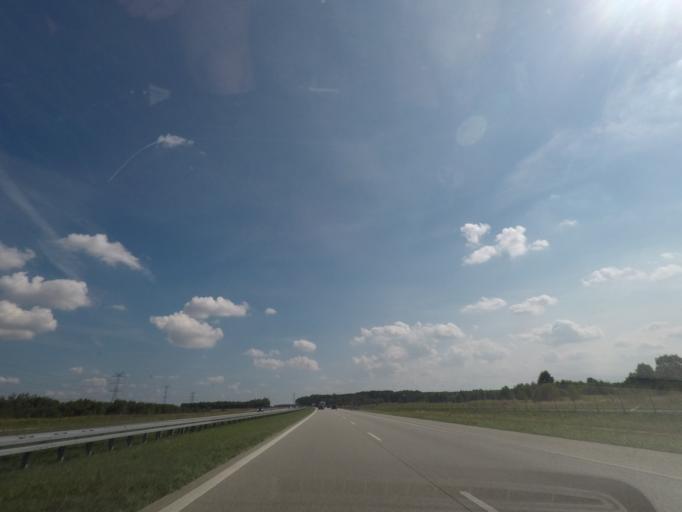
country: PL
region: Lodz Voivodeship
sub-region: Powiat lodzki wschodni
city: Tuszyn
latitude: 51.6133
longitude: 19.5710
